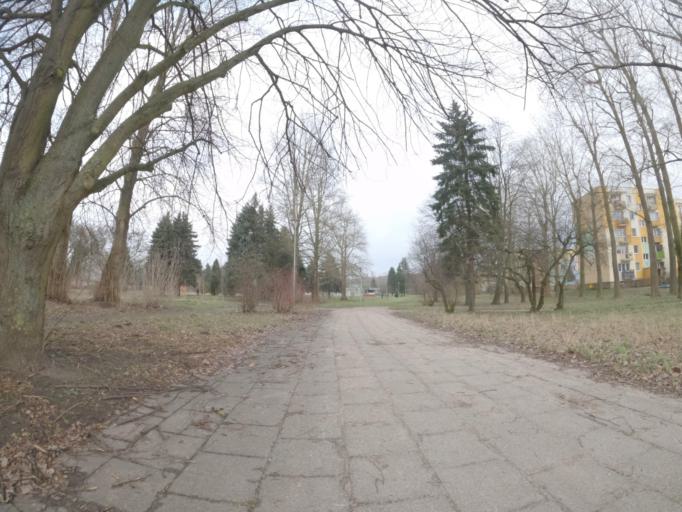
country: PL
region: West Pomeranian Voivodeship
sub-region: Koszalin
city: Koszalin
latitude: 54.2005
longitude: 16.2045
